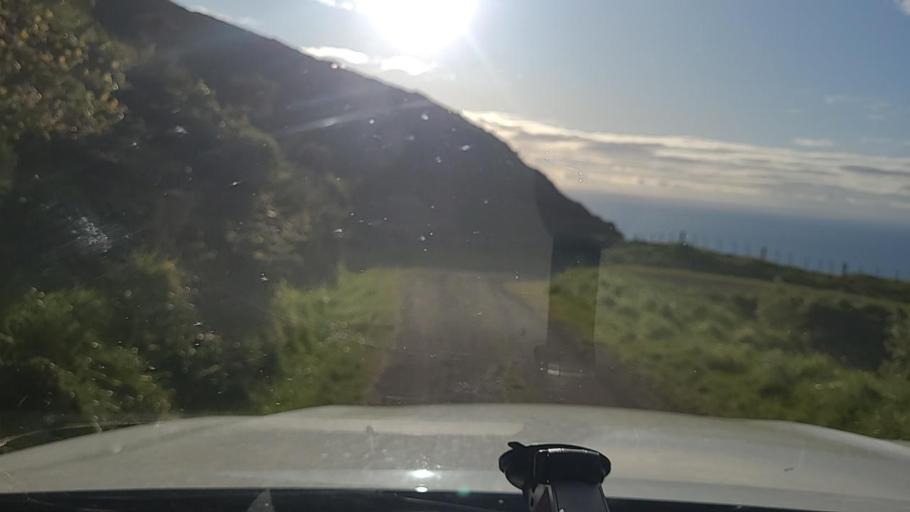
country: NZ
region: Gisborne
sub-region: Gisborne District
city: Gisborne
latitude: -38.9546
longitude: 177.8900
